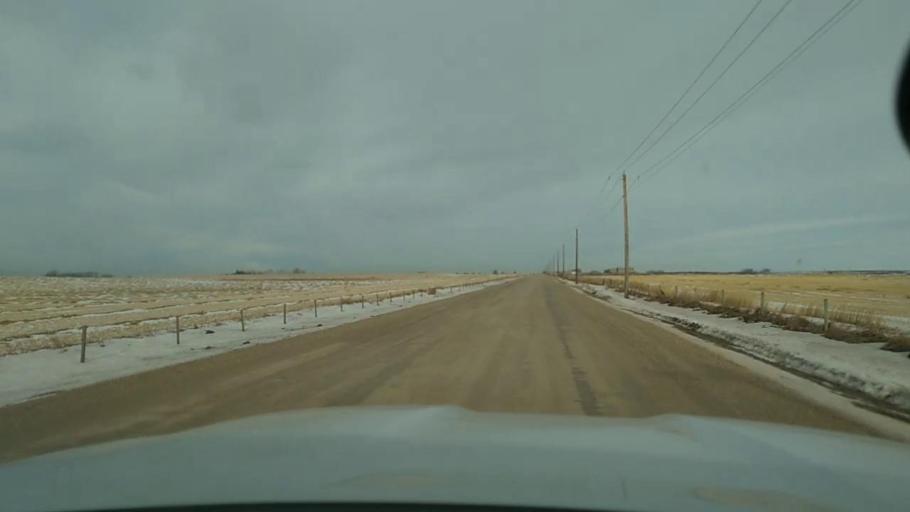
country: CA
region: Alberta
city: Airdrie
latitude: 51.2171
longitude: -113.9118
